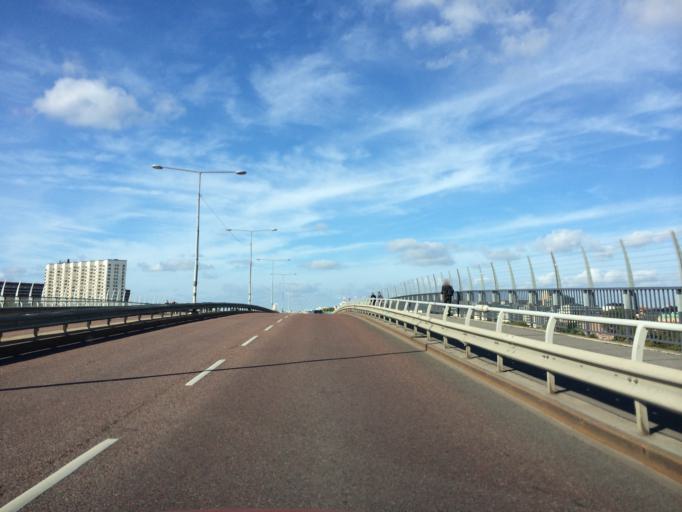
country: SE
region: Stockholm
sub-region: Stockholms Kommun
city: Arsta
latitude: 59.3234
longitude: 18.0288
